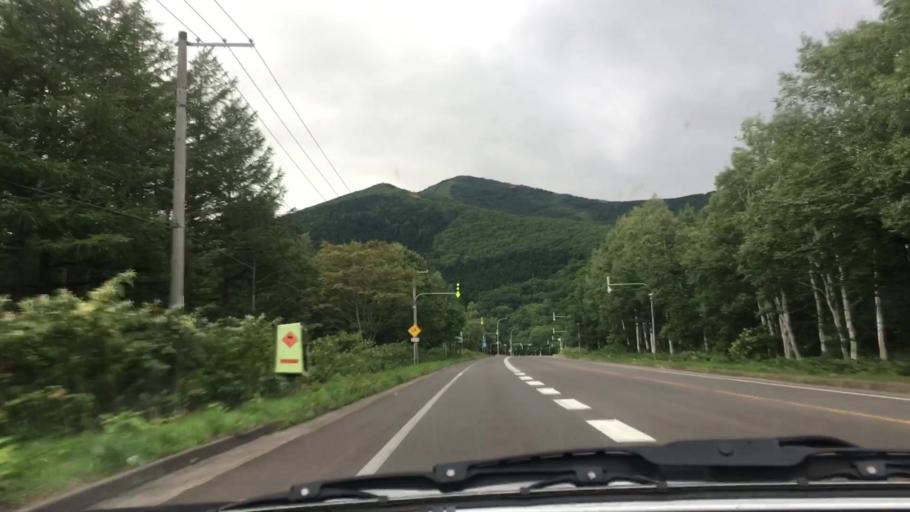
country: JP
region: Hokkaido
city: Otofuke
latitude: 43.1627
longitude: 142.8116
